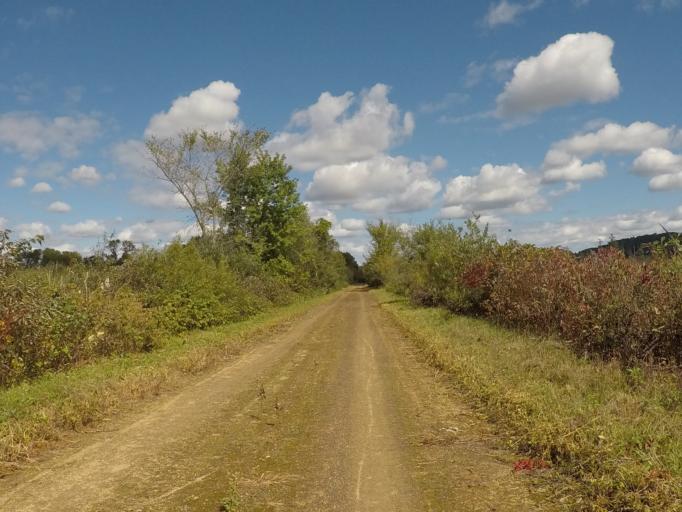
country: US
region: Wisconsin
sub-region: Richland County
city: Richland Center
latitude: 43.2568
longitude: -90.3026
